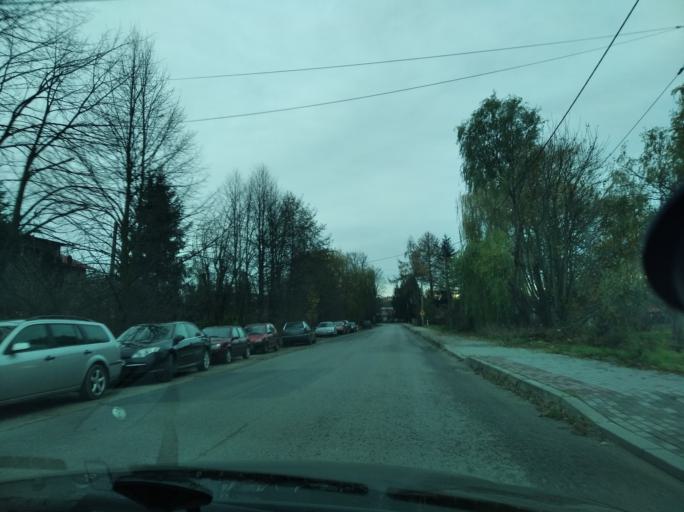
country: PL
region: Subcarpathian Voivodeship
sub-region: Powiat lancucki
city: Krzemienica
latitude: 50.0814
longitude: 22.1892
